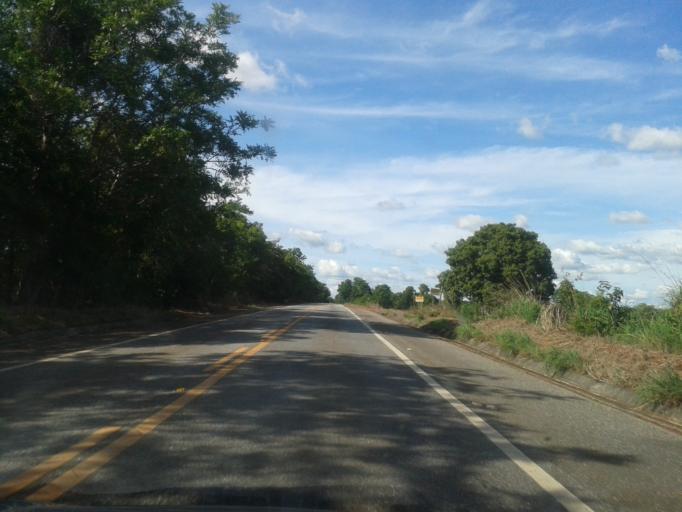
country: BR
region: Goias
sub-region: Mozarlandia
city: Mozarlandia
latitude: -14.9534
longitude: -50.5788
